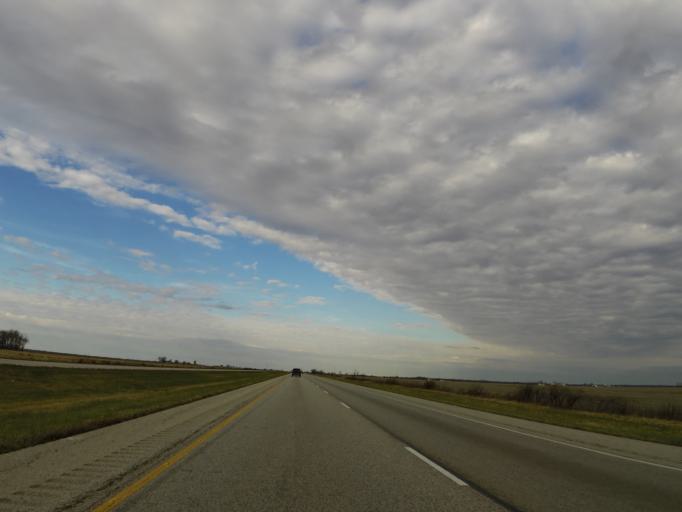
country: US
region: Illinois
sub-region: Washington County
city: Nashville
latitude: 38.4191
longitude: -89.4473
